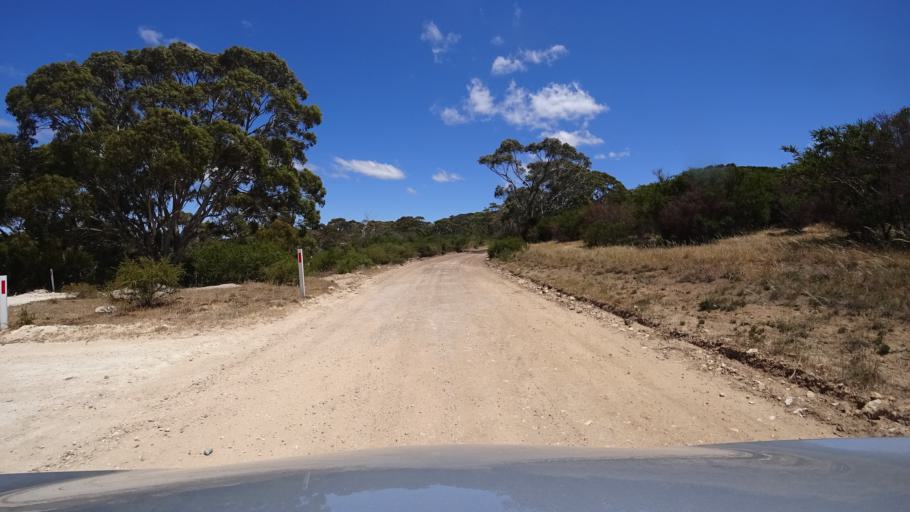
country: AU
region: South Australia
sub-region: Yankalilla
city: Normanville
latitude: -35.7846
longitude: 138.0653
